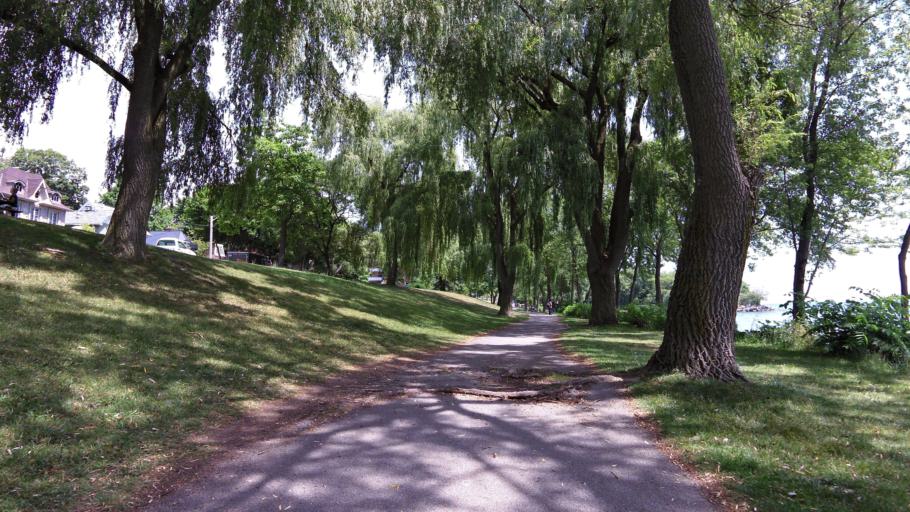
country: CA
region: Ontario
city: Etobicoke
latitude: 43.5883
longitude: -79.5330
